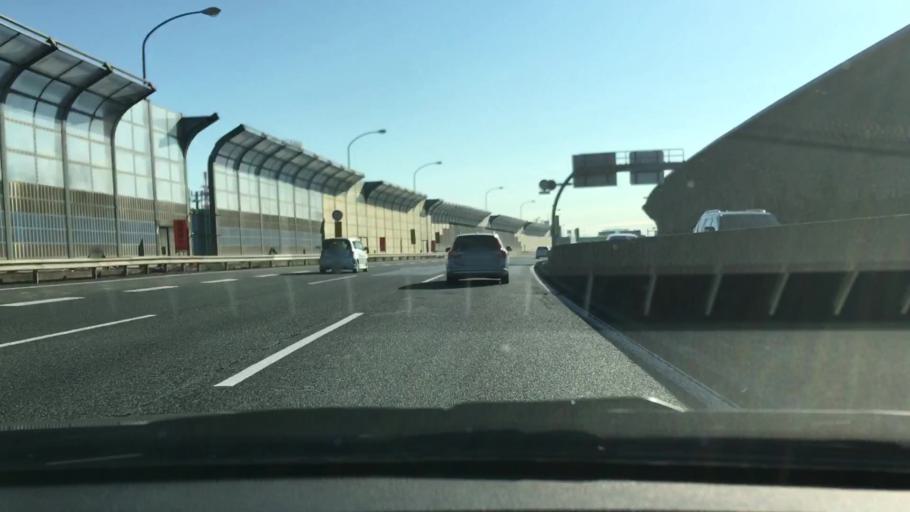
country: JP
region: Chiba
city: Funabashi
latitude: 35.6983
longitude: 139.9710
